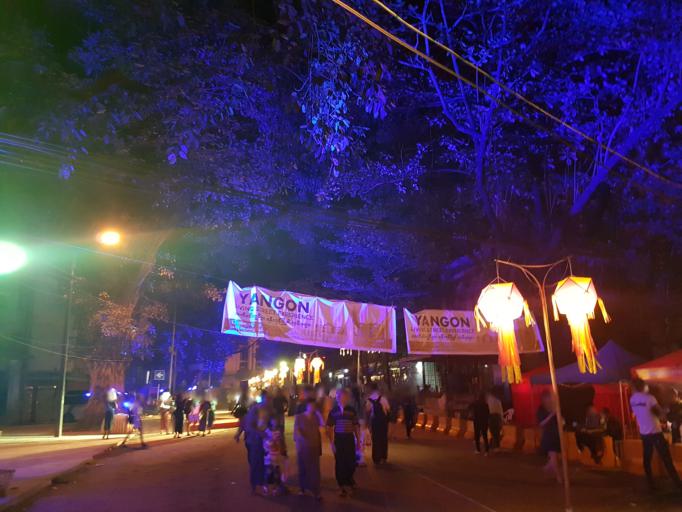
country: MM
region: Yangon
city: Yangon
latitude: 16.7708
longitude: 96.1600
